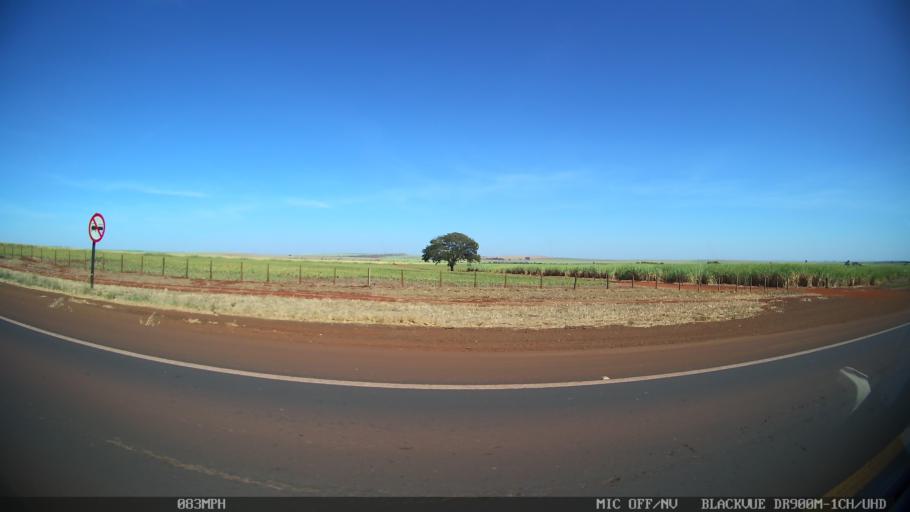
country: BR
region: Sao Paulo
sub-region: Ipua
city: Ipua
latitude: -20.4696
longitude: -48.1137
